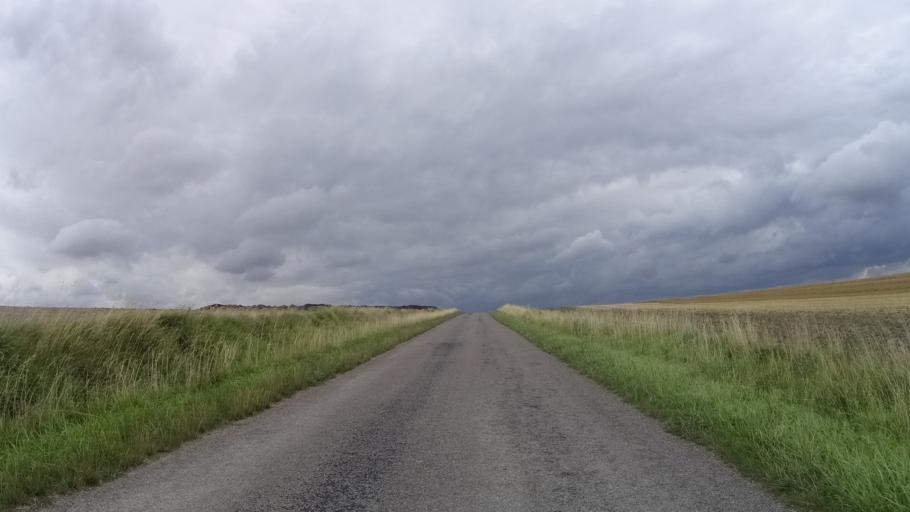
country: FR
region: Champagne-Ardenne
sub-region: Departement de l'Aube
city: Bouilly
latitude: 48.1490
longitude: 4.0353
